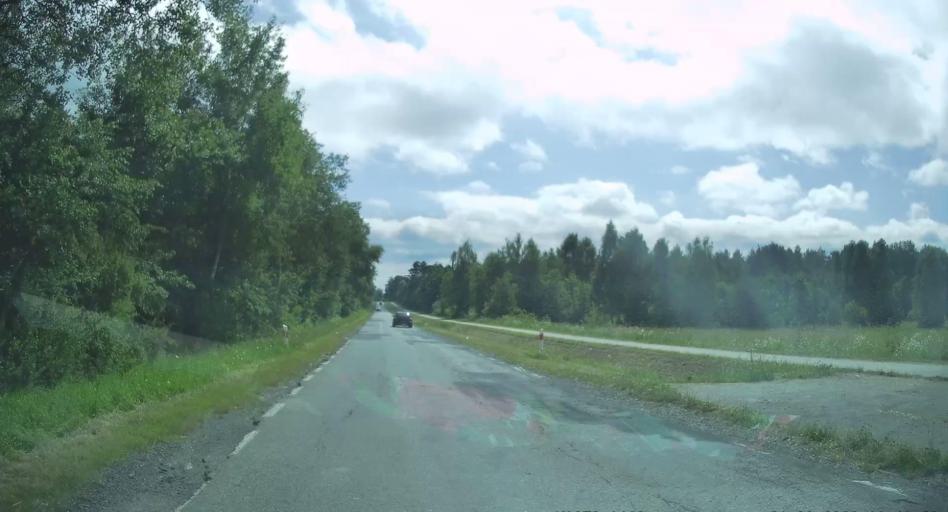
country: PL
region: Swietokrzyskie
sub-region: Powiat opatowski
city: Iwaniska
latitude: 50.7025
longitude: 21.3299
